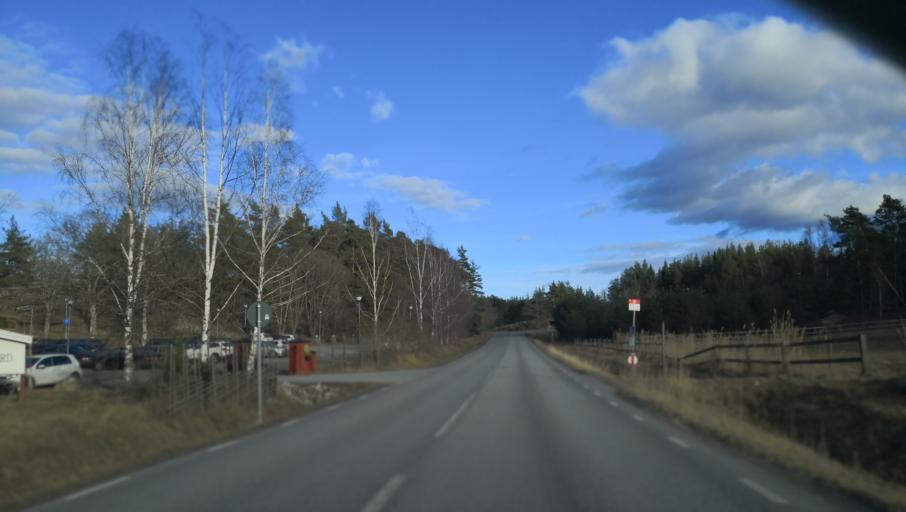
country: SE
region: Stockholm
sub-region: Varmdo Kommun
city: Gustavsberg
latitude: 59.3479
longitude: 18.3797
